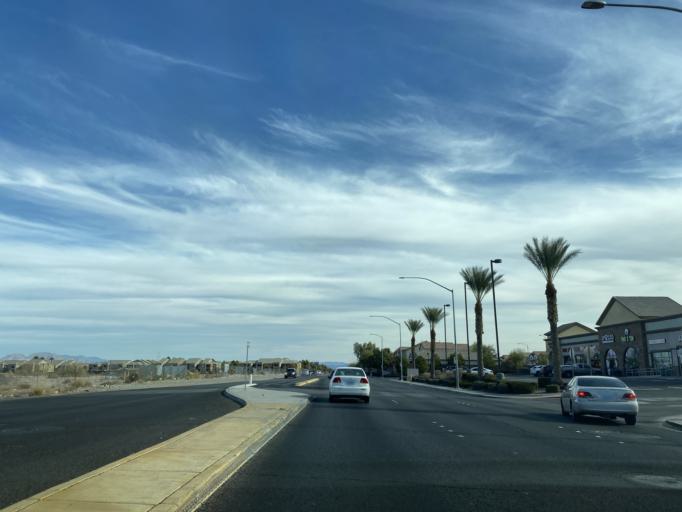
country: US
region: Nevada
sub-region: Clark County
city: Enterprise
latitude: 36.0558
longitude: -115.2423
